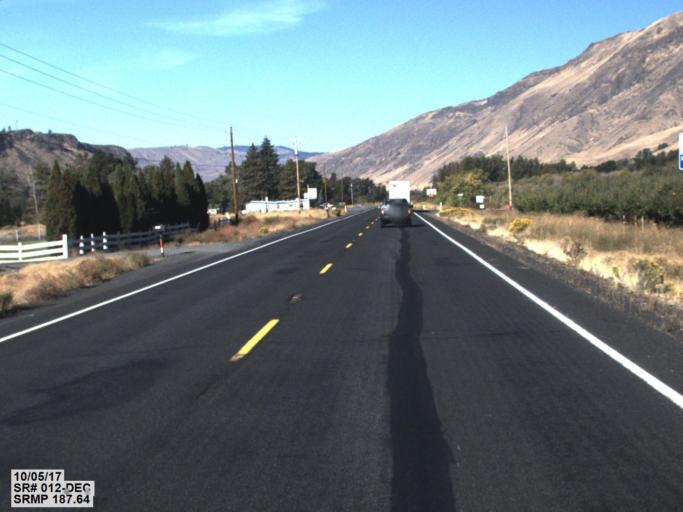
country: US
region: Washington
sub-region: Yakima County
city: Tieton
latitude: 46.7404
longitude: -120.7437
